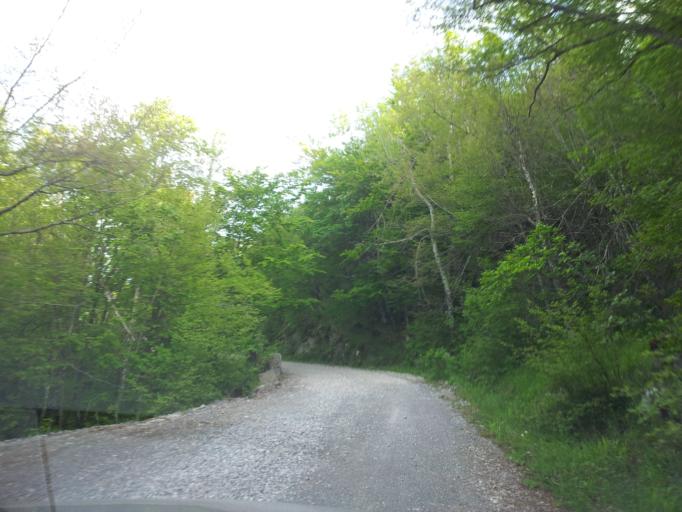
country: HR
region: Zadarska
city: Obrovac
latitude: 44.3018
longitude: 15.6624
